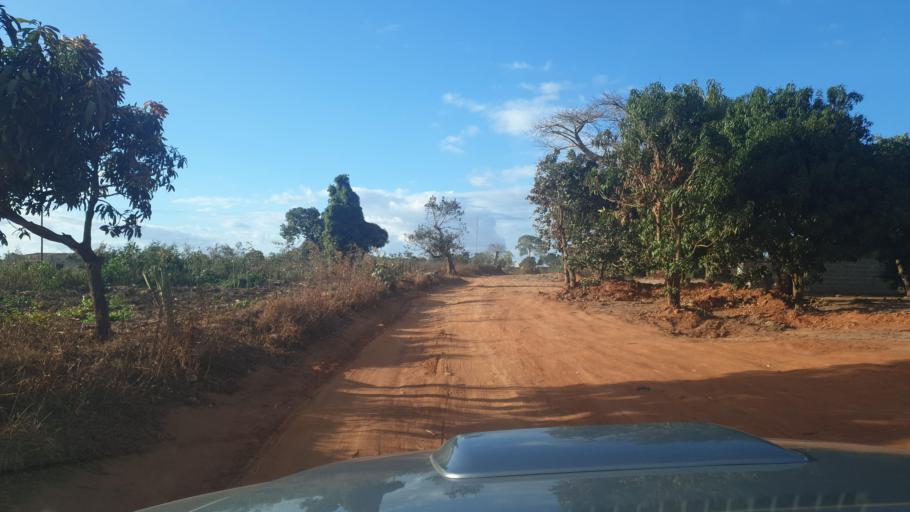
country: MZ
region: Nampula
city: Nampula
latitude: -15.1541
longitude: 39.2656
